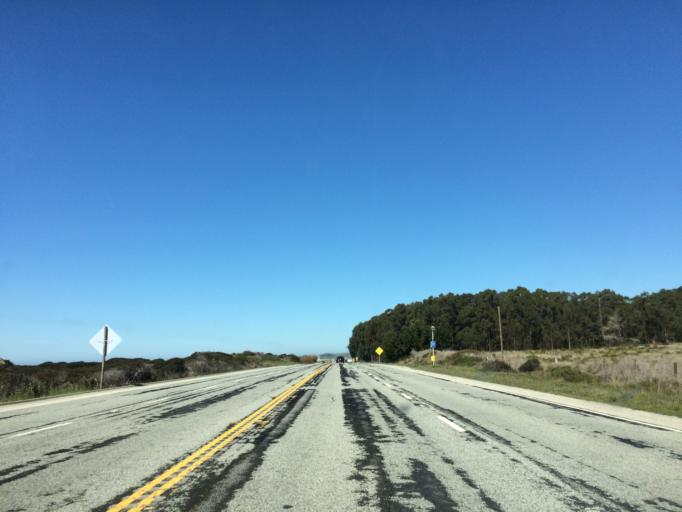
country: US
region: California
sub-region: Santa Cruz County
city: Bonny Doon
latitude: 37.1531
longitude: -122.3517
